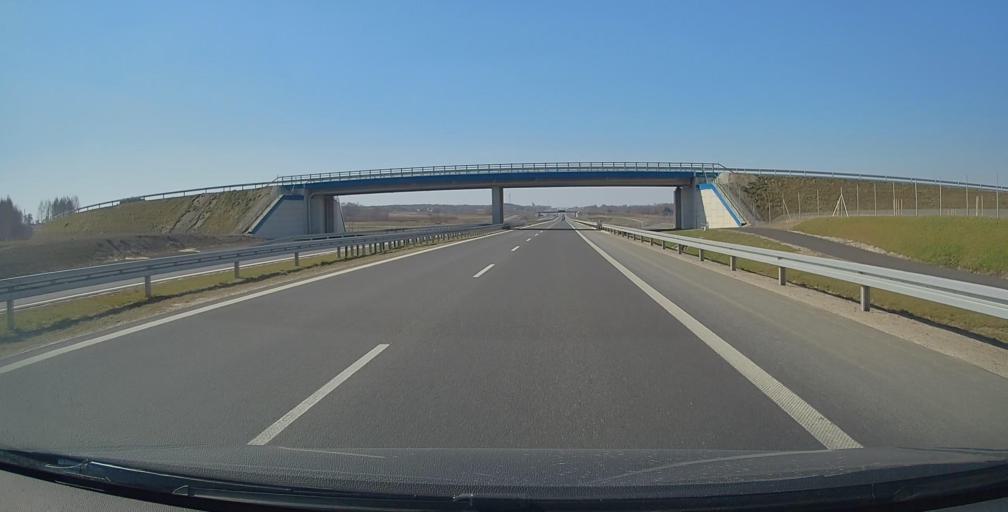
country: PL
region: Subcarpathian Voivodeship
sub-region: Powiat rzeszowski
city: Gorno
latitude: 50.3148
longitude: 22.1677
